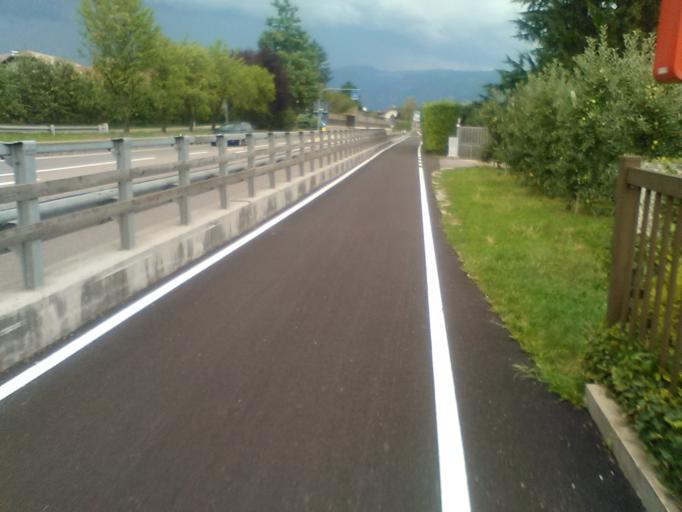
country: IT
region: Trentino-Alto Adige
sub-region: Bolzano
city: San Michele
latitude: 46.4492
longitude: 11.2652
